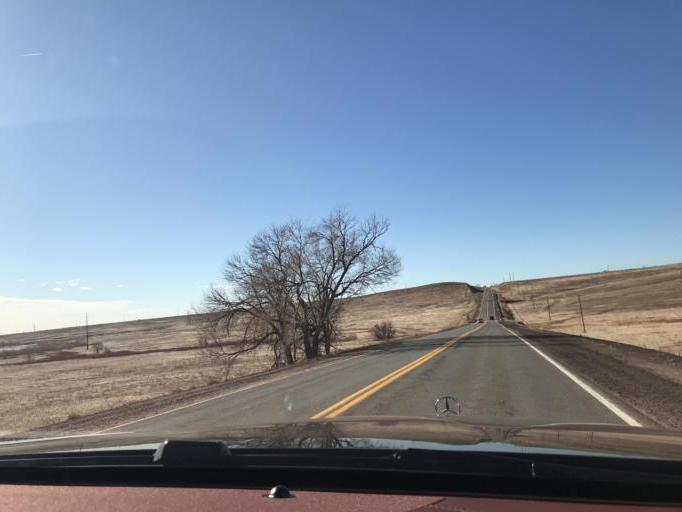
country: US
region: Colorado
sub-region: Boulder County
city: Superior
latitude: 39.9038
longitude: -105.1657
